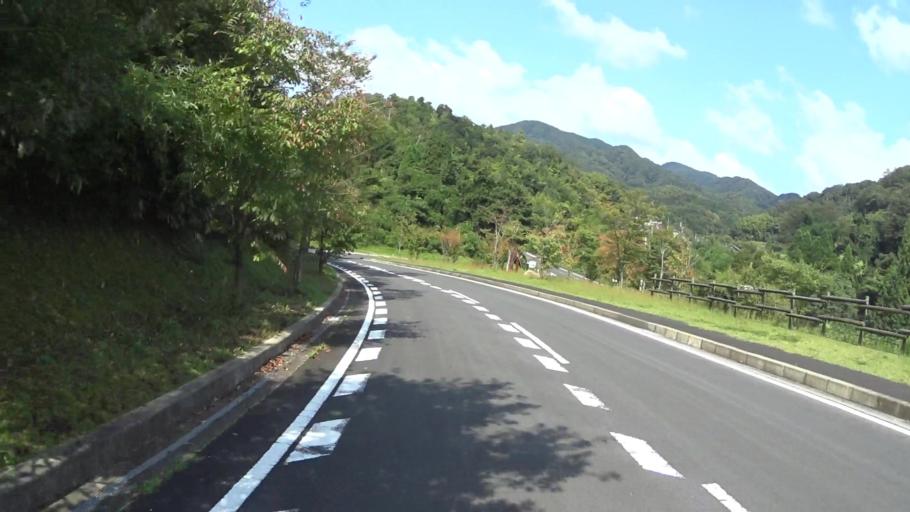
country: JP
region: Kyoto
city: Miyazu
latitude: 35.6287
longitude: 135.2342
